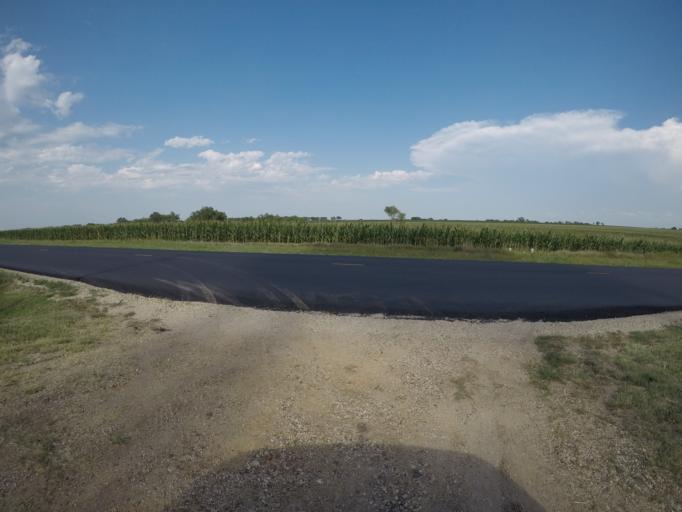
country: US
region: Kansas
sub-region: Washington County
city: Washington
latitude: 39.9337
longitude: -96.8627
